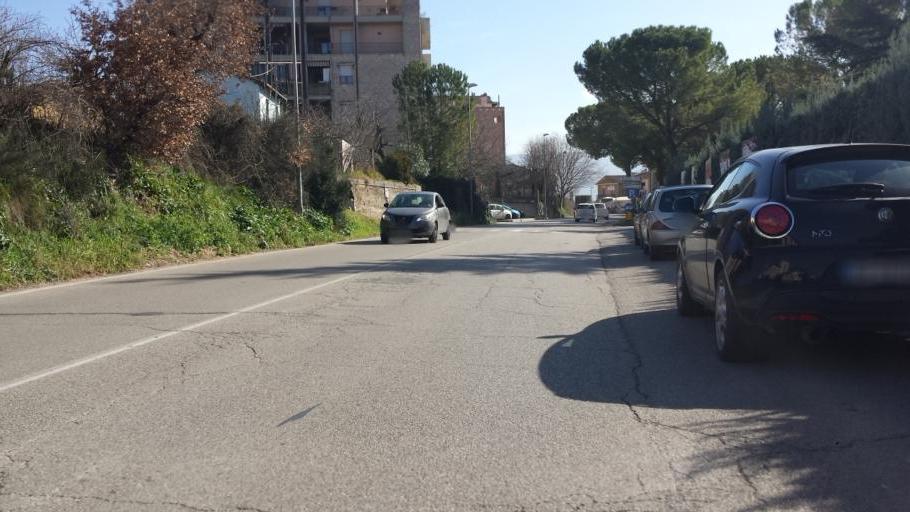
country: IT
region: Umbria
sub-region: Provincia di Terni
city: Terni
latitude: 42.5863
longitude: 12.6100
